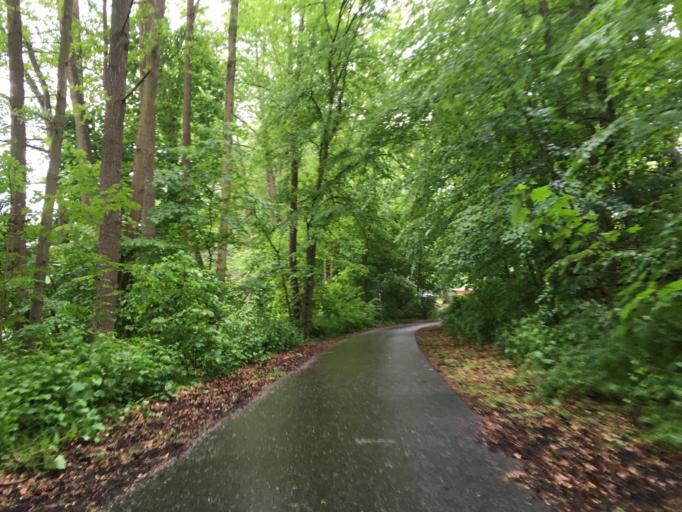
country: DE
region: Brandenburg
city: Eberswalde
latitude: 52.8413
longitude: 13.7857
